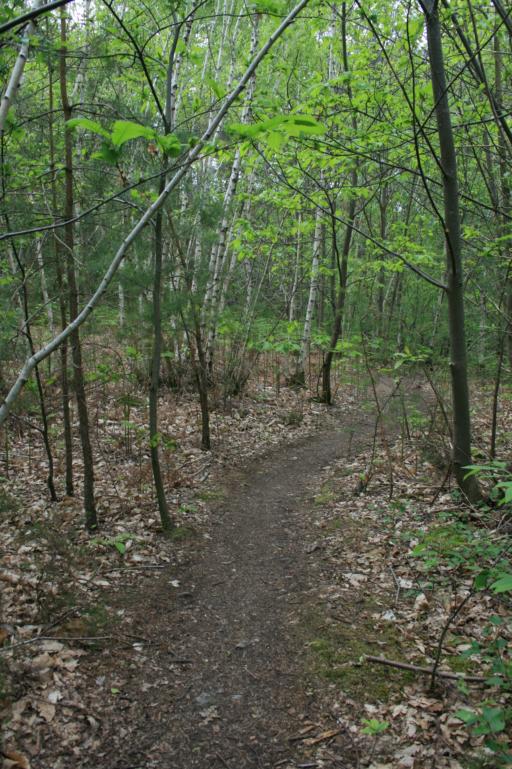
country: FR
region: Ile-de-France
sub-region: Departement du Val-d'Oise
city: Menucourt
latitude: 49.0078
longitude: 1.9959
